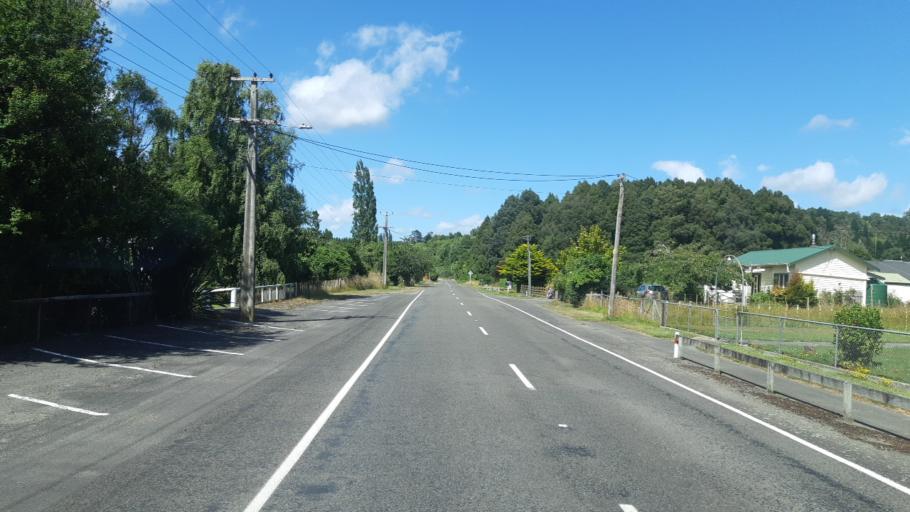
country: NZ
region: Manawatu-Wanganui
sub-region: Palmerston North City
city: Palmerston North
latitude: -40.1737
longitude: 175.7947
